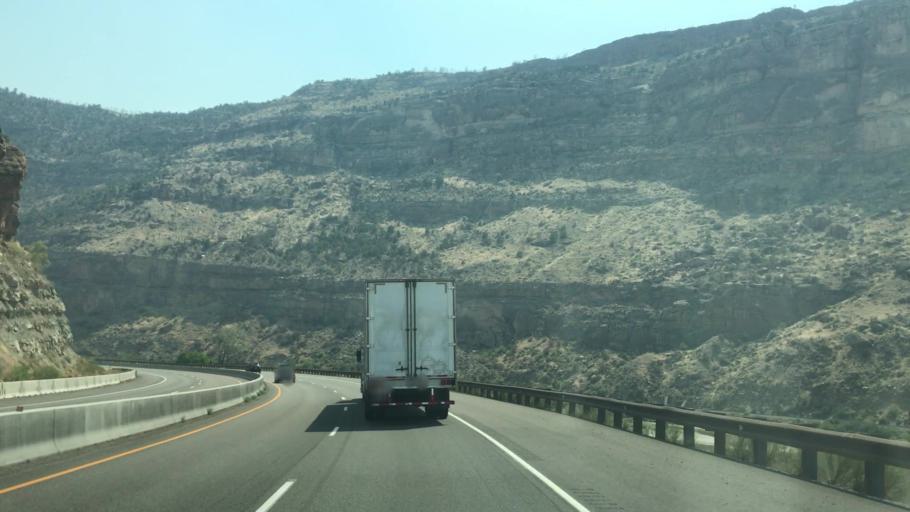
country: US
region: Colorado
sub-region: Mesa County
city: Palisade
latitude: 39.2343
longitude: -108.2725
